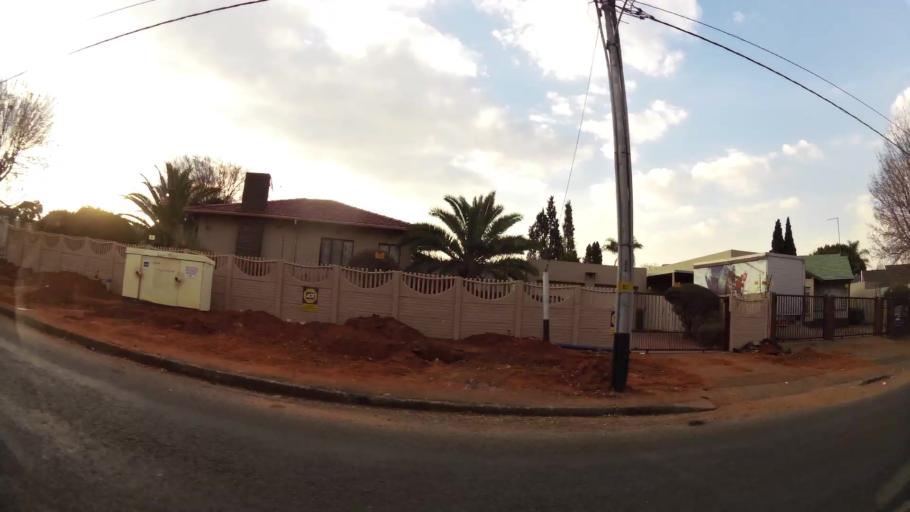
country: ZA
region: Gauteng
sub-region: Ekurhuleni Metropolitan Municipality
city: Germiston
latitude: -26.1815
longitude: 28.1743
